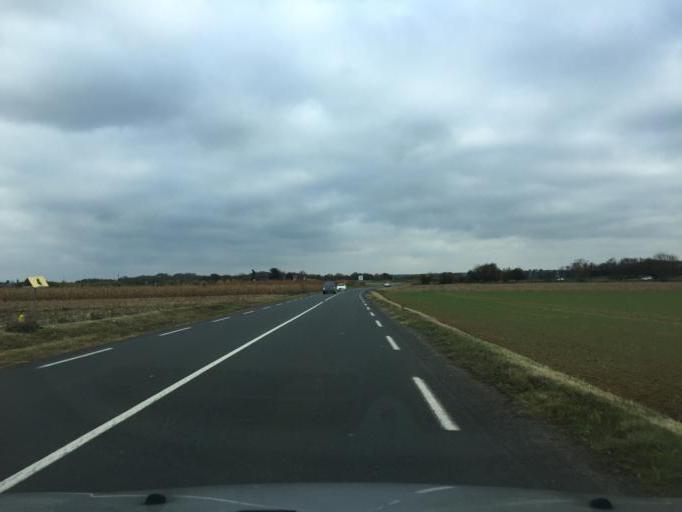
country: FR
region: Rhone-Alpes
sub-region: Departement de l'Ain
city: Frans
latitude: 45.9861
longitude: 4.7888
